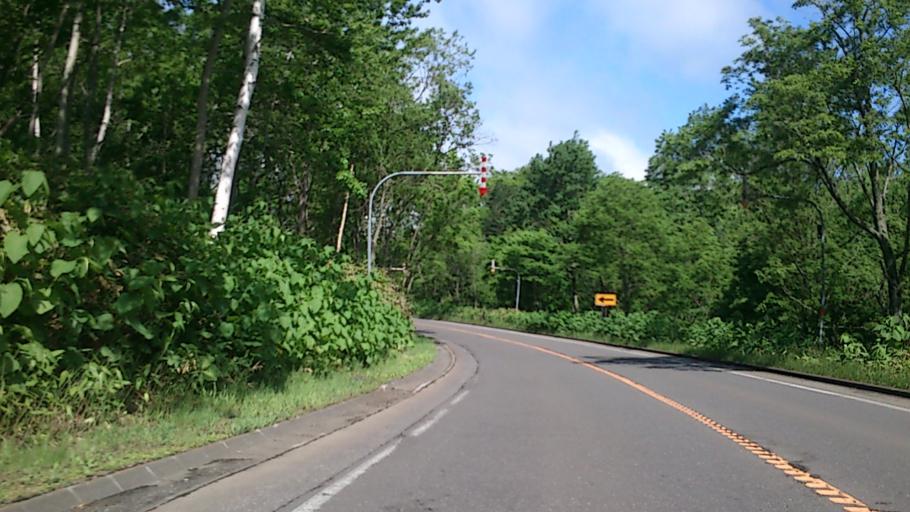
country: JP
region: Hokkaido
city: Shiraoi
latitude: 42.7183
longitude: 141.2151
